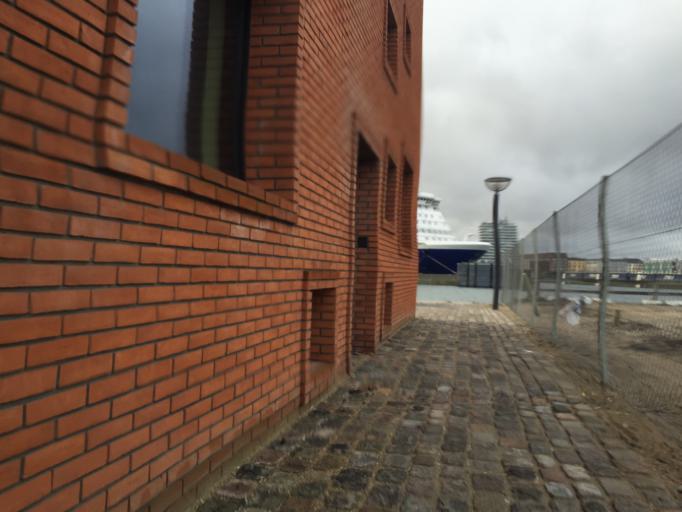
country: DK
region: Capital Region
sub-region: Kobenhavn
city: Christianshavn
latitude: 55.7024
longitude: 12.6001
